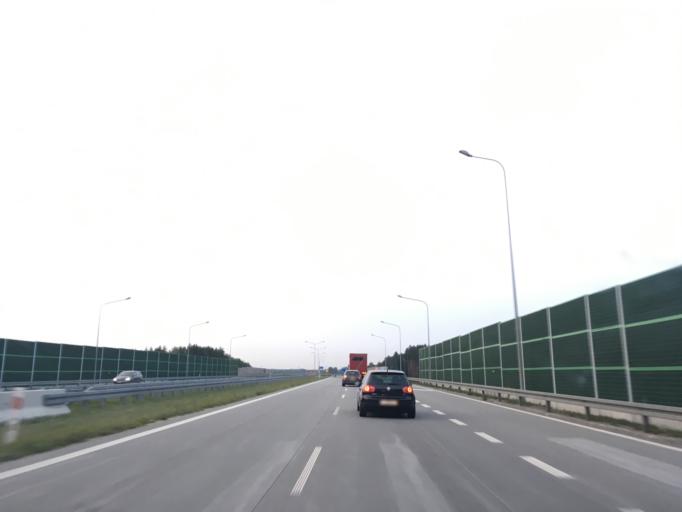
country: PL
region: Lodz Voivodeship
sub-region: Powiat lodzki wschodni
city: Tuszyn
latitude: 51.6317
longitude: 19.5686
